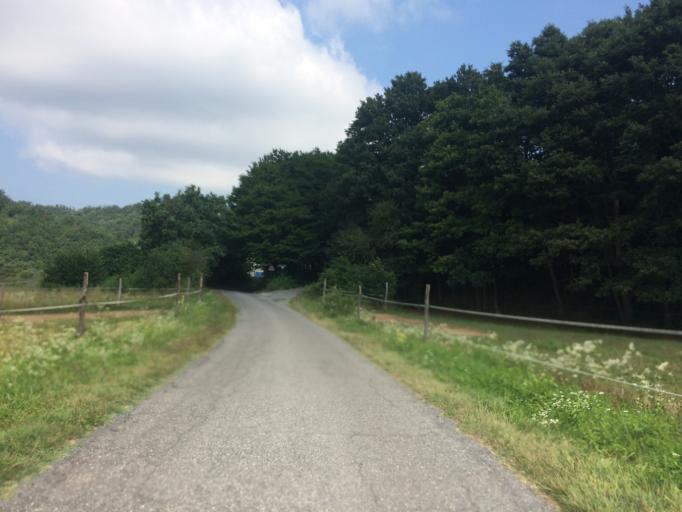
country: IT
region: Liguria
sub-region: Provincia di Savona
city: Piana Crixia
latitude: 44.4649
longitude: 8.3492
